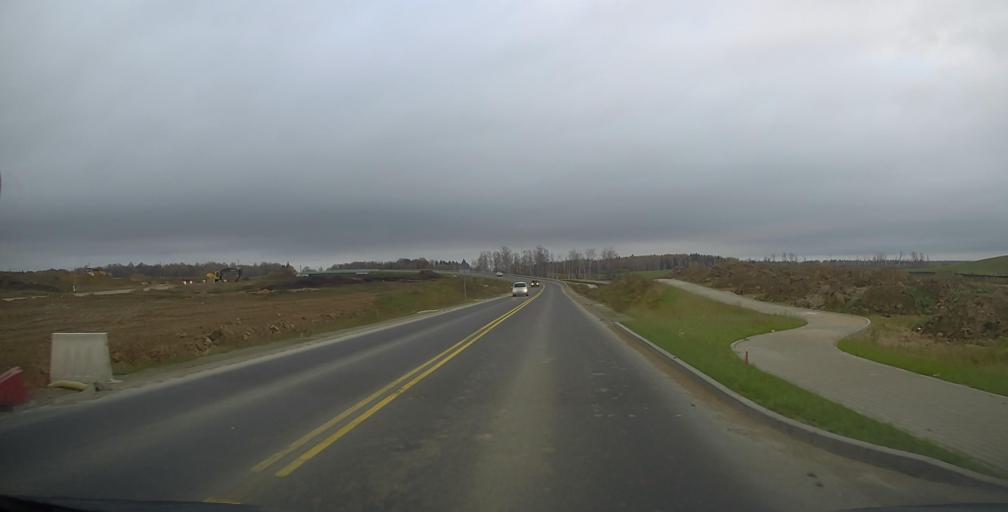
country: PL
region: Warmian-Masurian Voivodeship
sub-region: Powiat elcki
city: Elk
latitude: 53.8536
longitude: 22.4905
